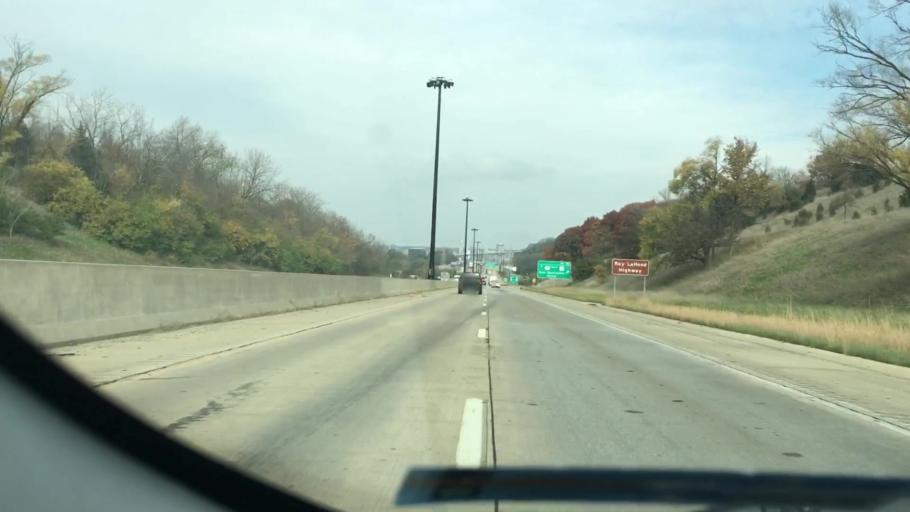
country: US
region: Illinois
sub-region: Tazewell County
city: East Peoria
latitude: 40.6576
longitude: -89.5642
